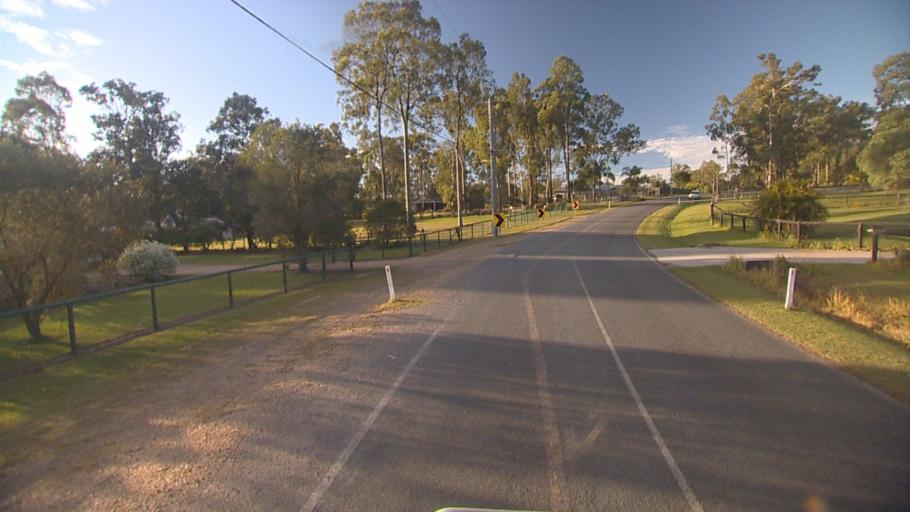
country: AU
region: Queensland
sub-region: Logan
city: Waterford West
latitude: -27.7311
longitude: 153.1375
